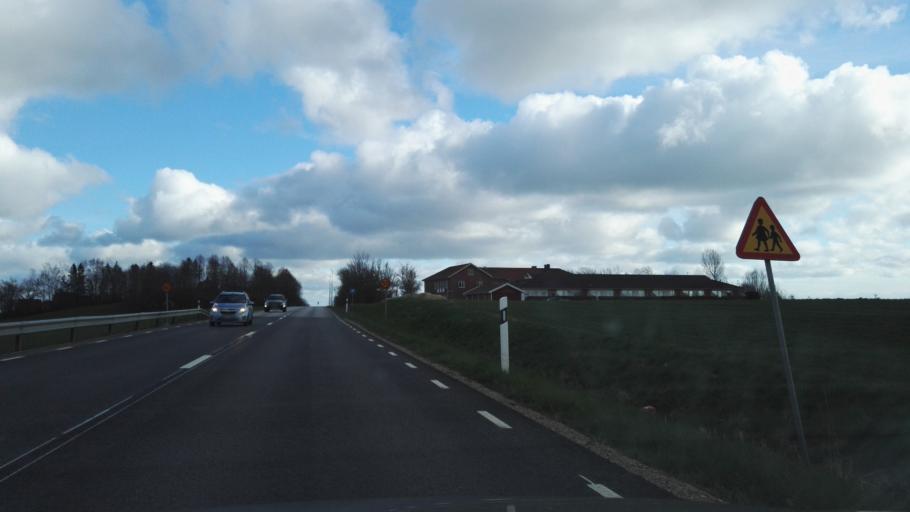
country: SE
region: Skane
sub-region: Ystads Kommun
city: Ystad
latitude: 55.5069
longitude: 13.7942
